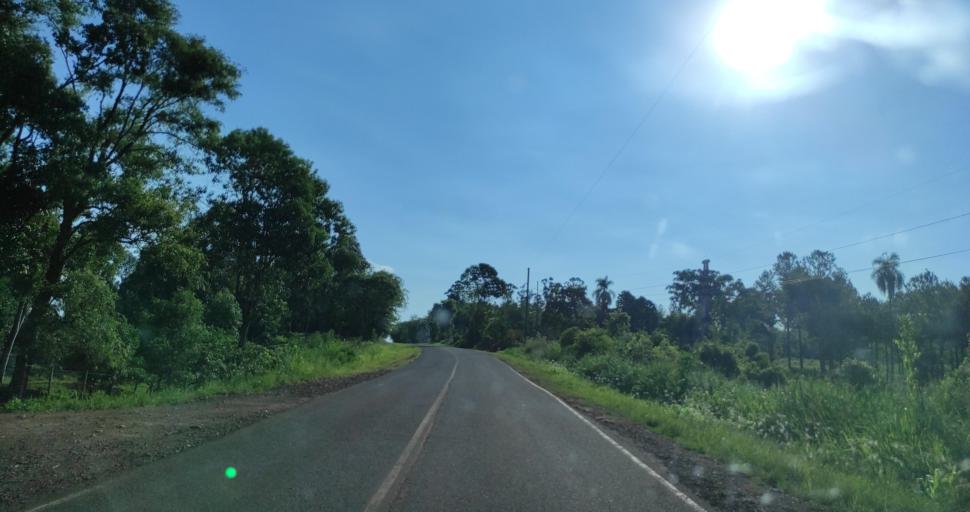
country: AR
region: Misiones
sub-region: Departamento de Eldorado
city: Eldorado
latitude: -26.3882
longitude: -54.3536
